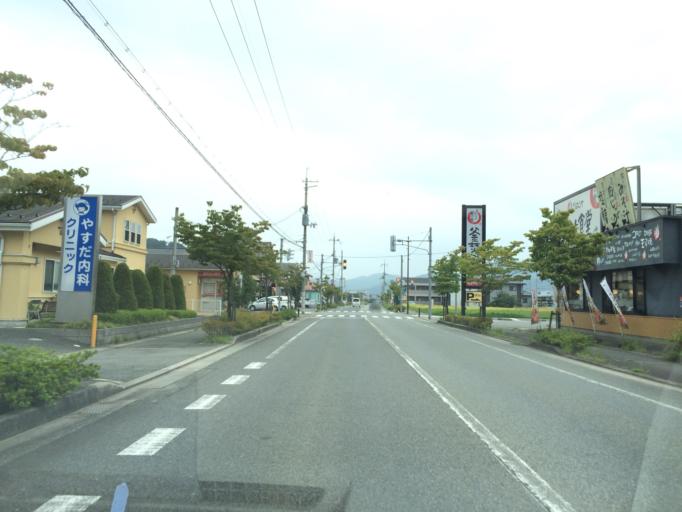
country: JP
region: Hyogo
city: Toyooka
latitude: 35.5366
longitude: 134.8087
